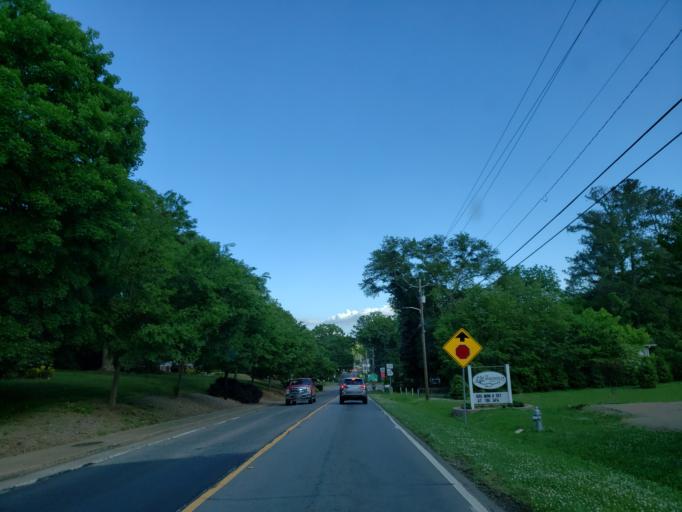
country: US
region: Georgia
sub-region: Cherokee County
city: Canton
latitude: 34.3178
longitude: -84.5543
